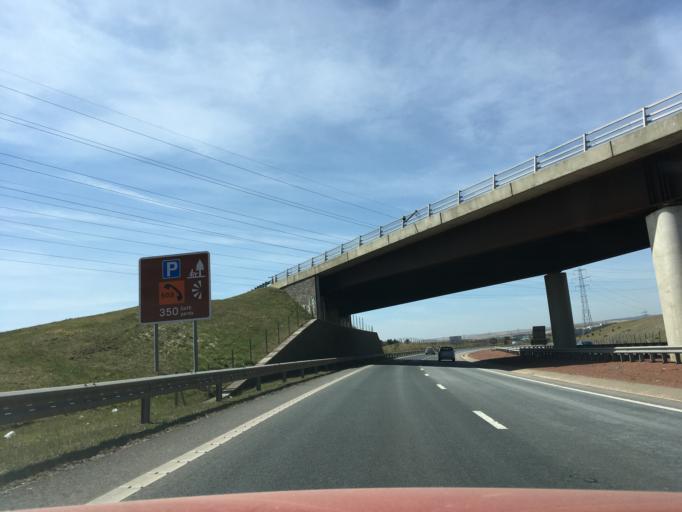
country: GB
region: Wales
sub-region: Blaenau Gwent
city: Brynmawr
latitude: 51.8065
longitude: -3.1942
